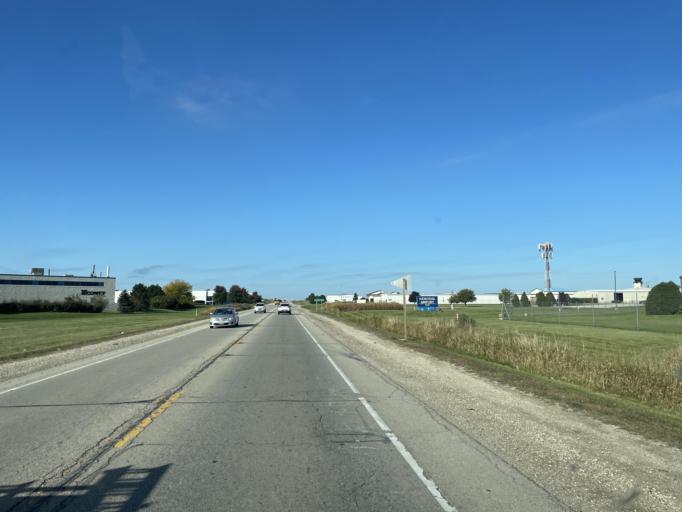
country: US
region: Wisconsin
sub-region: Kenosha County
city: Pleasant Prairie
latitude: 42.5893
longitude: -87.9206
